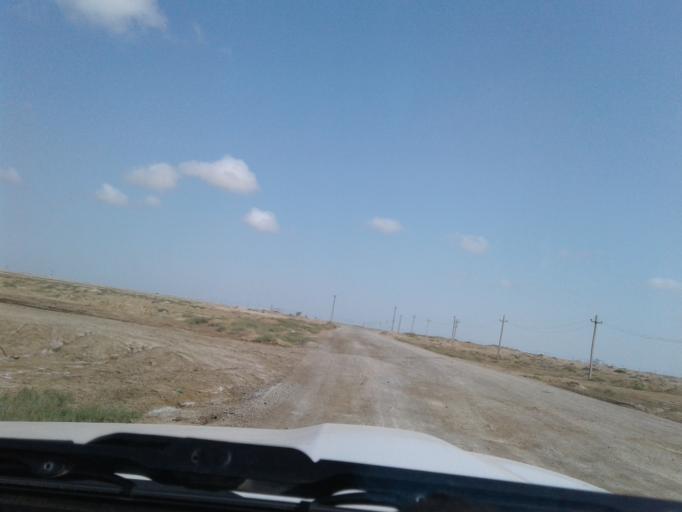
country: IR
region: Golestan
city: Gomishan
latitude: 37.7112
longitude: 53.9409
